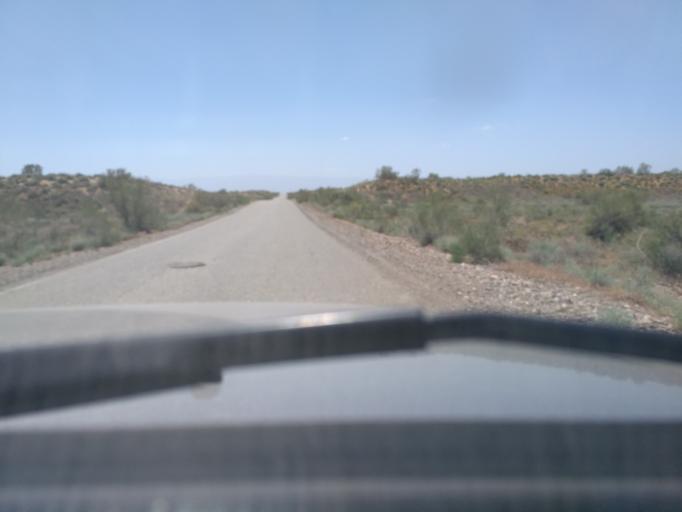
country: KZ
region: Ongtustik Qazaqstan
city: Sholaqqkorghan
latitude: 44.1983
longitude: 68.9143
